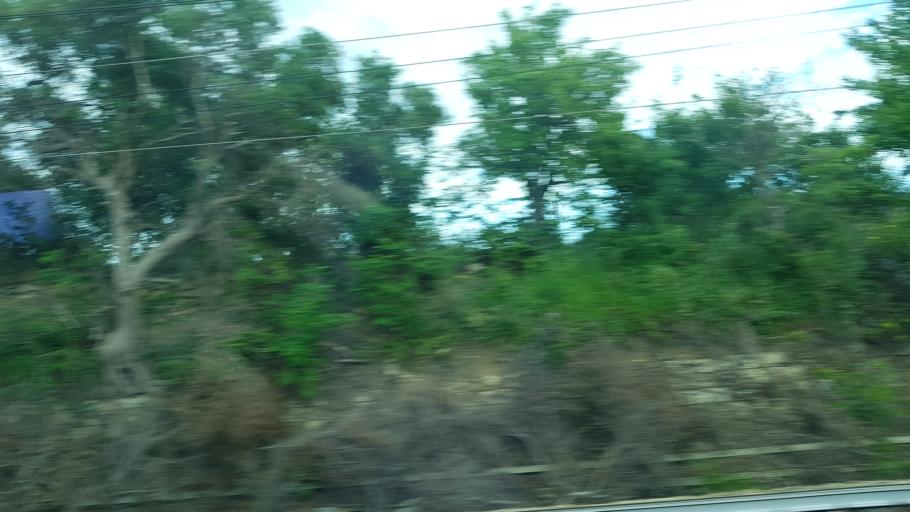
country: IT
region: Apulia
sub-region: Provincia di Brindisi
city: Brindisi
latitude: 40.6293
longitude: 17.9163
